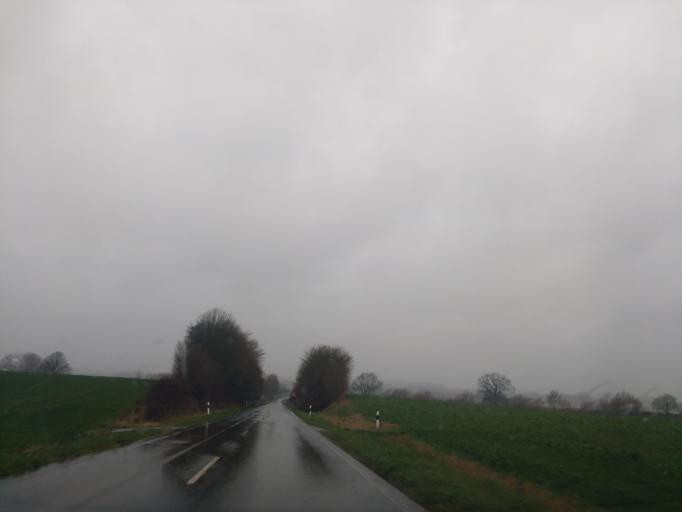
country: DE
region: Schleswig-Holstein
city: Blekendorf
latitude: 54.2966
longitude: 10.6731
